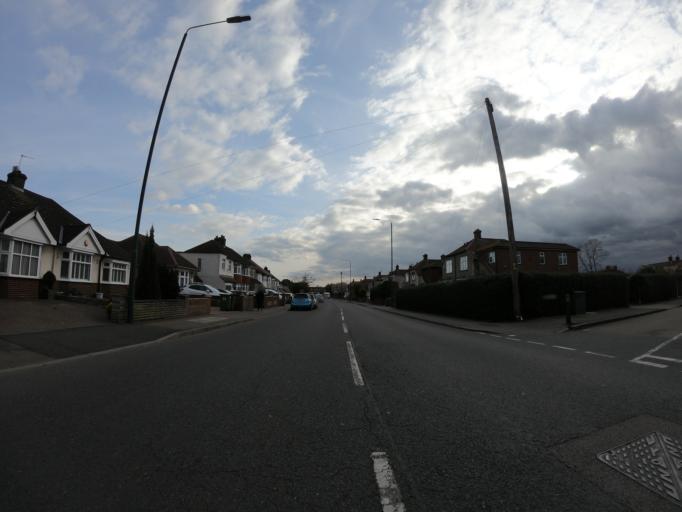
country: GB
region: England
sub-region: Greater London
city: Bexleyheath
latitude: 51.4696
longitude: 0.1438
